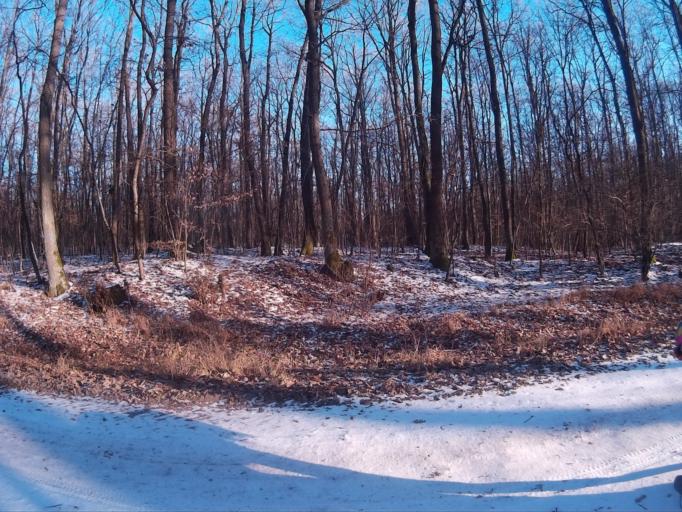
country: HU
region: Borsod-Abauj-Zemplen
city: Putnok
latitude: 48.4516
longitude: 20.4698
